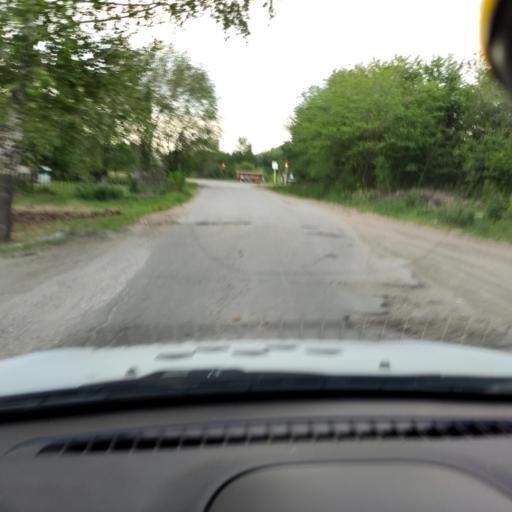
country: RU
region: Samara
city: Podstepki
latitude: 53.5830
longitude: 49.2294
